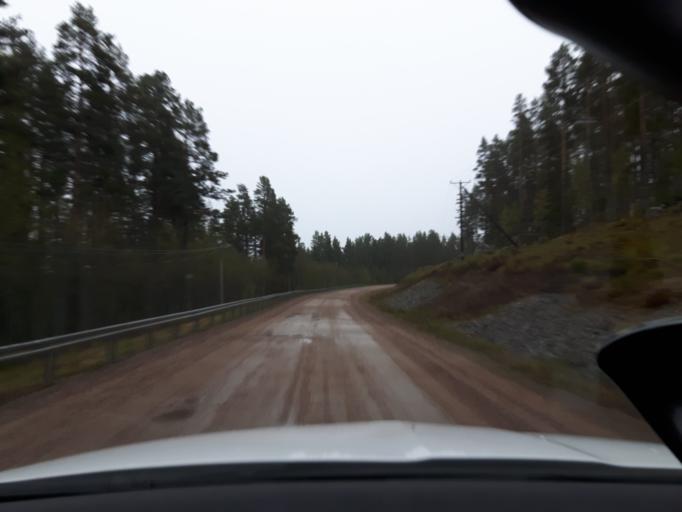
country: SE
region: Vaesternorrland
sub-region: Ange Kommun
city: Ange
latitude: 62.1664
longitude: 15.6560
